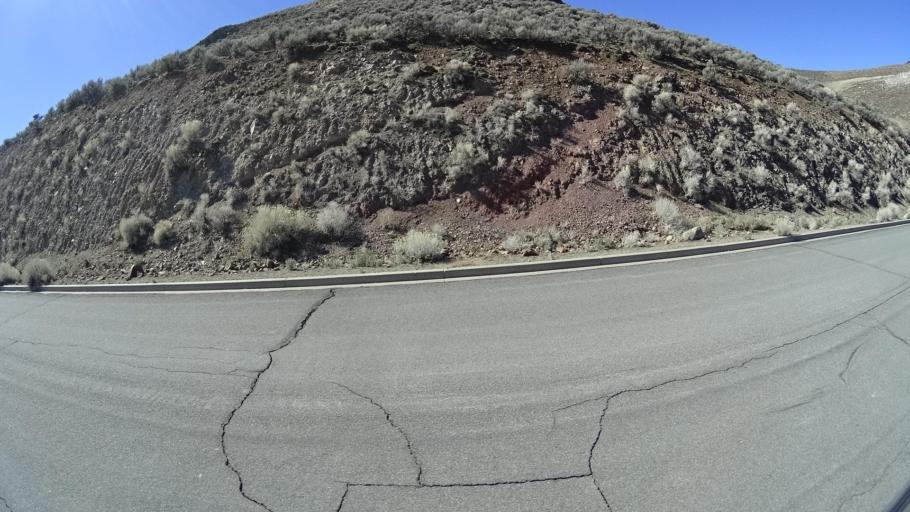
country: US
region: Nevada
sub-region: Washoe County
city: Sparks
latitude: 39.4777
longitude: -119.7254
